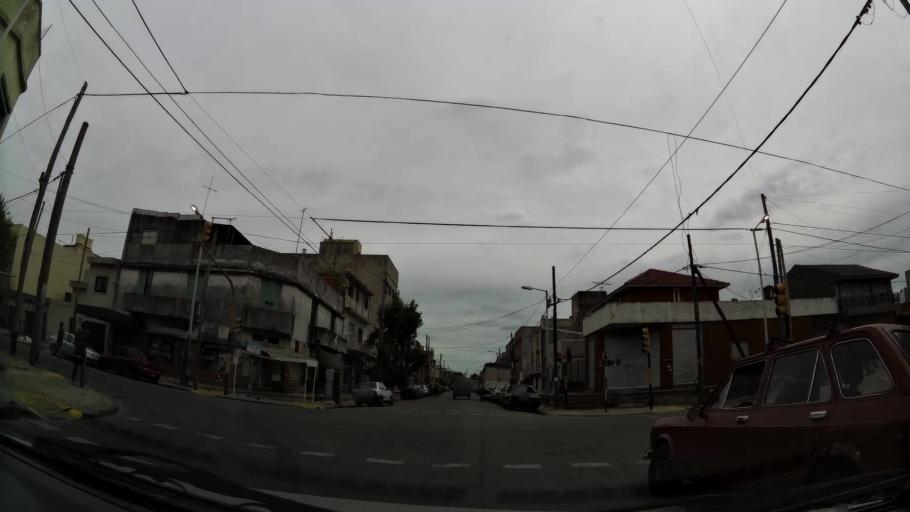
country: AR
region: Buenos Aires
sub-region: Partido de Avellaneda
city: Avellaneda
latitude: -34.6543
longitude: -58.3464
